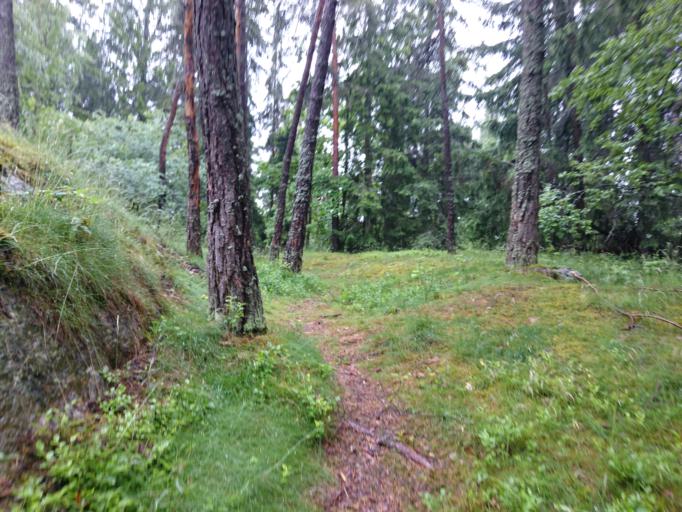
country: SE
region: Stockholm
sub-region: Huddinge Kommun
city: Segeltorp
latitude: 59.2696
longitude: 17.9288
